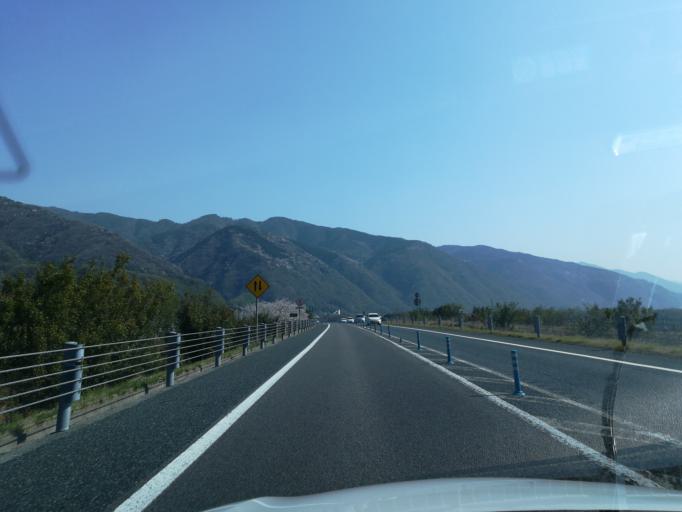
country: JP
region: Tokushima
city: Ikedacho
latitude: 34.0403
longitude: 133.9085
